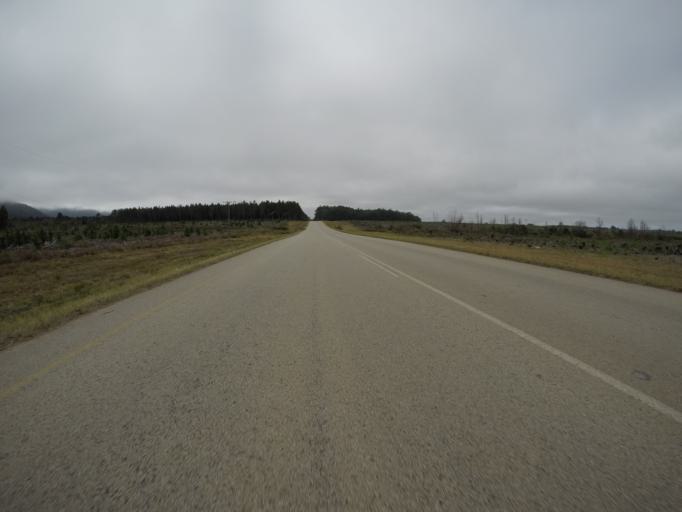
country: ZA
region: Eastern Cape
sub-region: Cacadu District Municipality
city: Kareedouw
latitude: -33.9940
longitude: 24.1021
